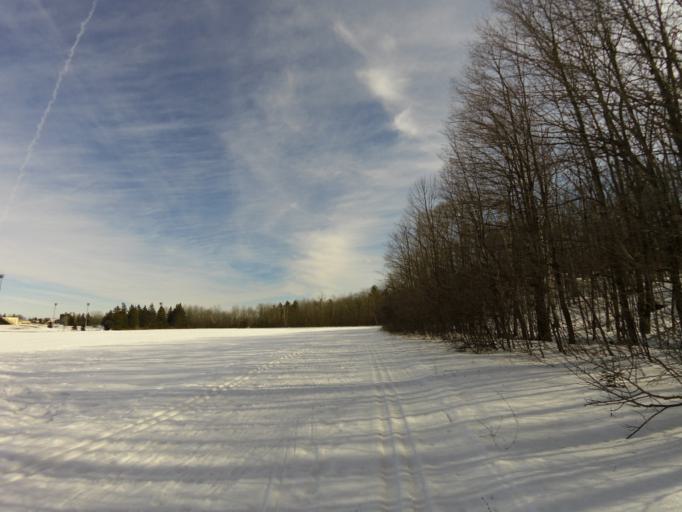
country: CA
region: Quebec
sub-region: Outaouais
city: Gatineau
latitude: 45.4609
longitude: -75.7782
